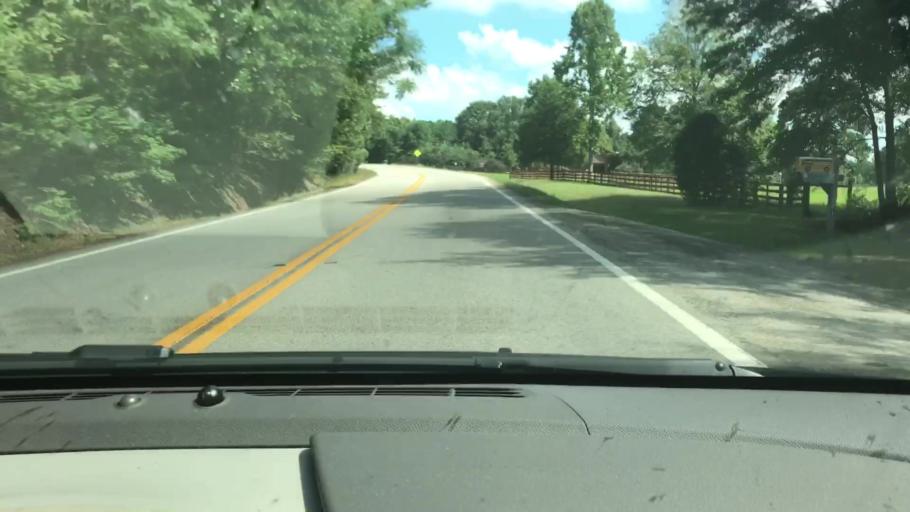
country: US
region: Georgia
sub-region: Troup County
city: La Grange
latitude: 32.9484
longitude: -85.0181
